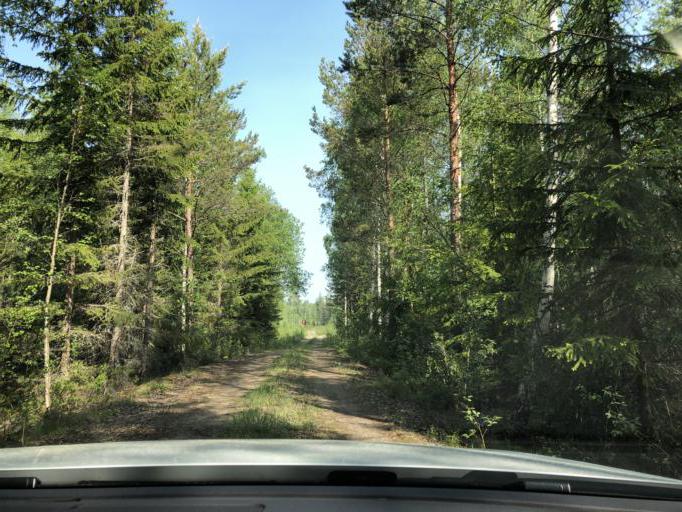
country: SE
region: Dalarna
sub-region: Avesta Kommun
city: Horndal
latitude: 60.2224
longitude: 16.5143
